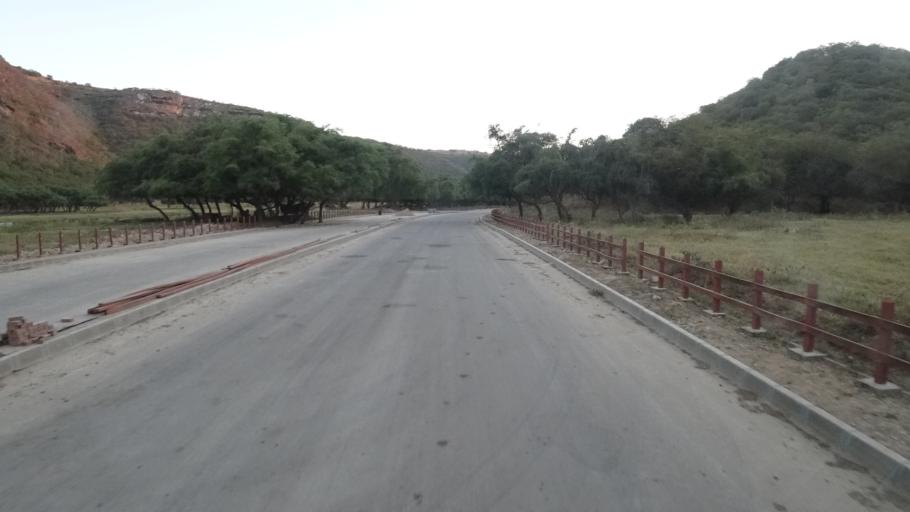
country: OM
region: Zufar
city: Salalah
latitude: 17.0982
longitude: 54.4500
